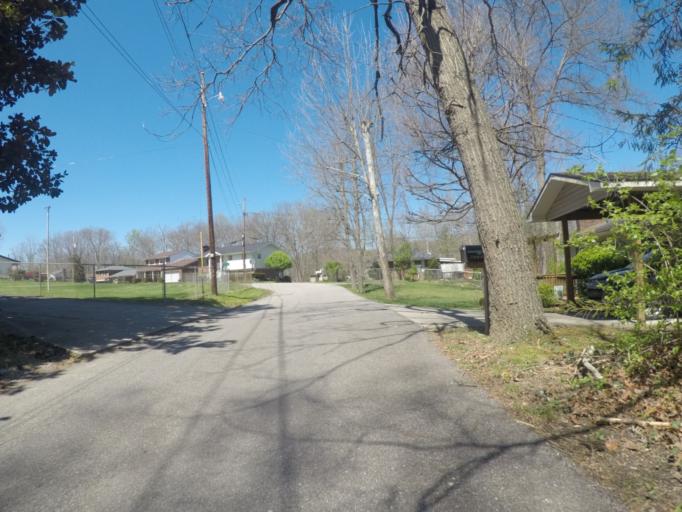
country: US
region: West Virginia
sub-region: Cabell County
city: Pea Ridge
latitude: 38.4204
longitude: -82.3121
